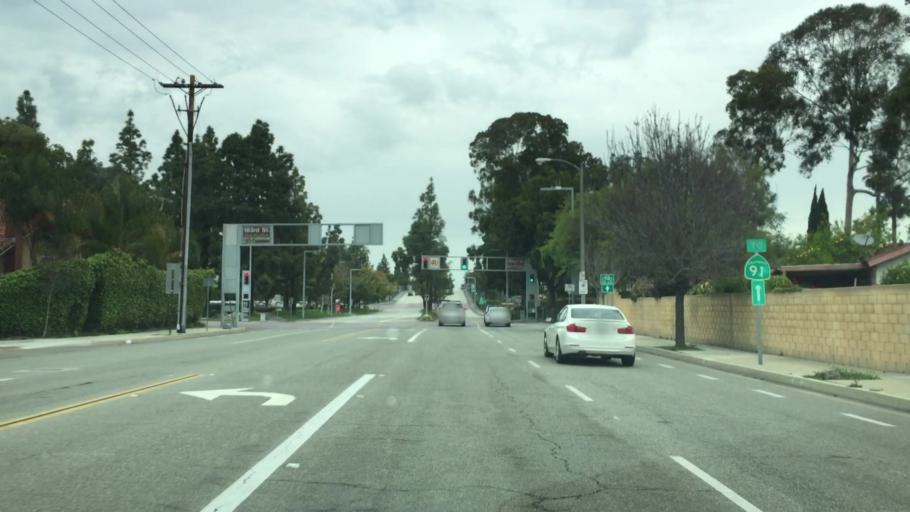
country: US
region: California
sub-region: Los Angeles County
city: Cerritos
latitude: 33.8653
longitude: -118.0550
